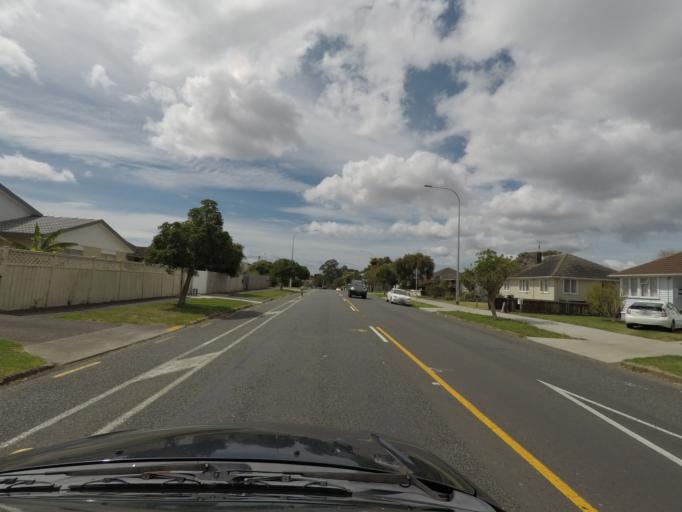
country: NZ
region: Auckland
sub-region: Auckland
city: Auckland
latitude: -36.9024
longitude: 174.7297
